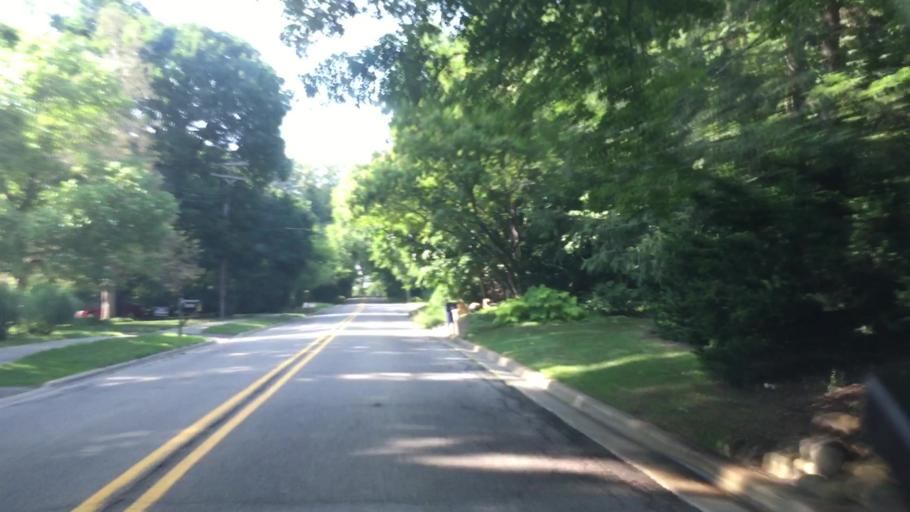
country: US
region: Michigan
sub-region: Oakland County
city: Franklin
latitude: 42.5357
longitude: -83.2956
